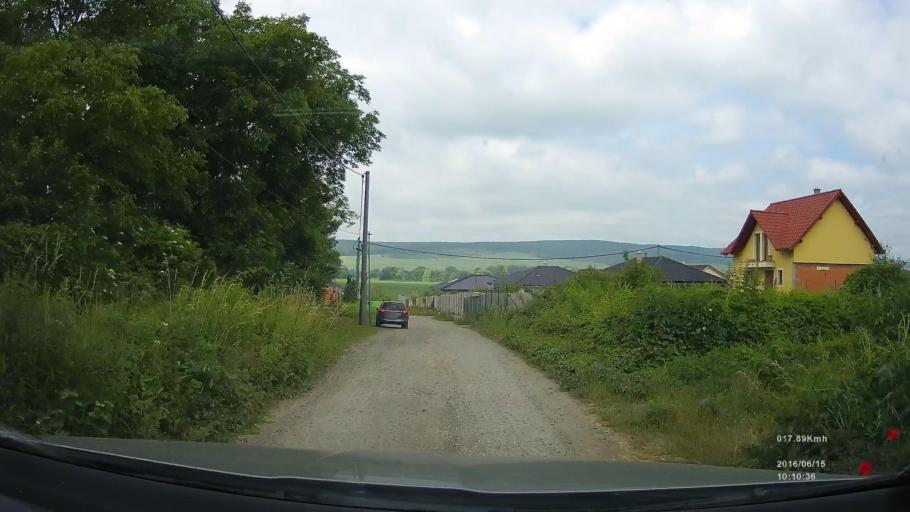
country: SK
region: Kosicky
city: Kosice
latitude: 48.7548
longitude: 21.3403
